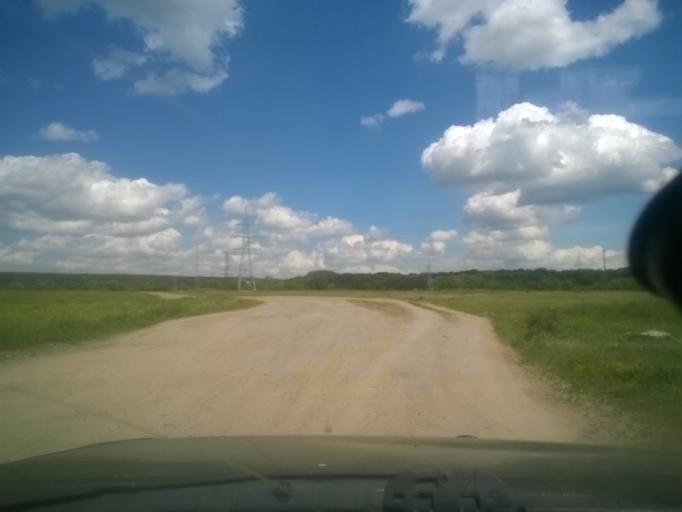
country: RU
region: Kursk
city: Kursk
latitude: 51.6791
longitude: 36.1125
